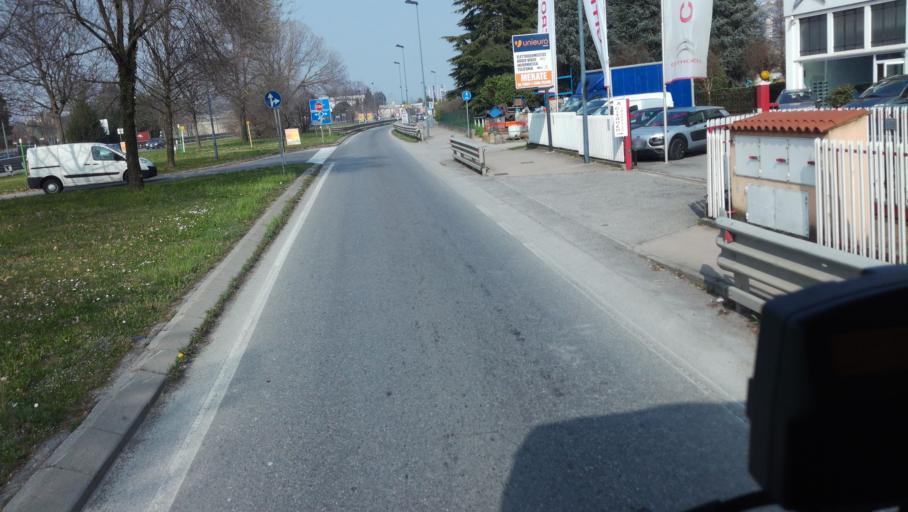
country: IT
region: Lombardy
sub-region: Provincia di Lecco
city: Osnago
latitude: 45.6704
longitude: 9.3899
